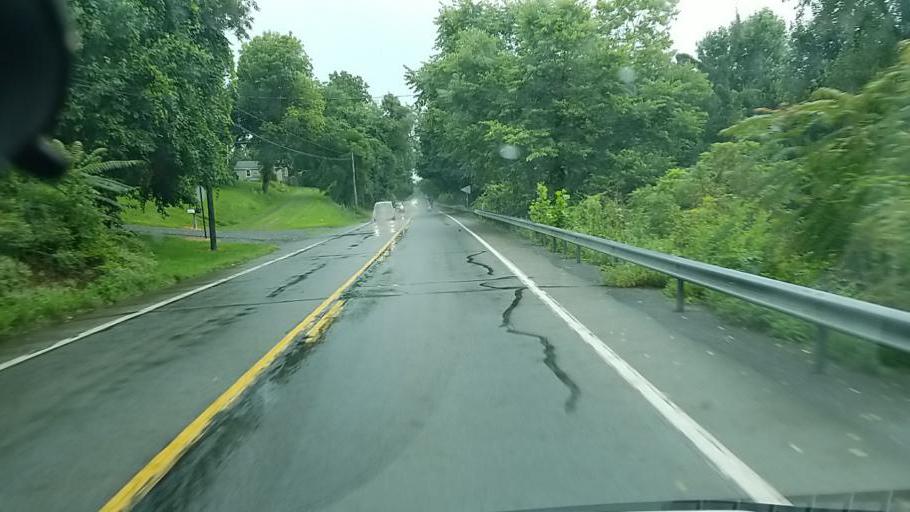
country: US
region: Pennsylvania
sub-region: Dauphin County
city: Millersburg
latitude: 40.5161
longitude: -76.9700
